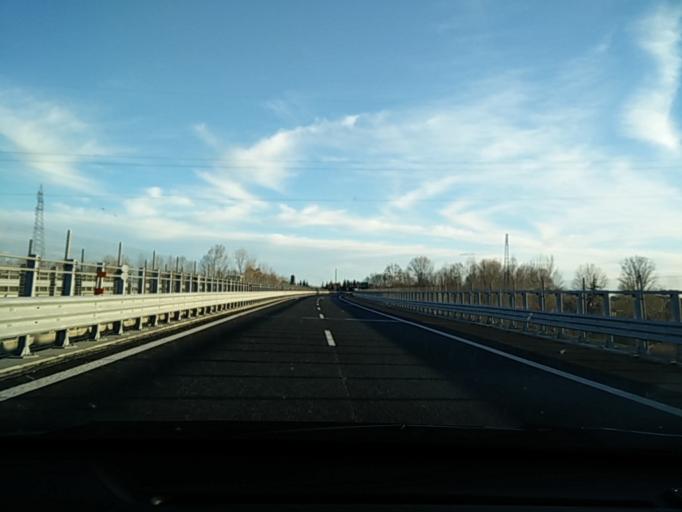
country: IT
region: Friuli Venezia Giulia
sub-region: Provincia di Udine
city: Tavagnacco
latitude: 46.1192
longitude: 13.2051
